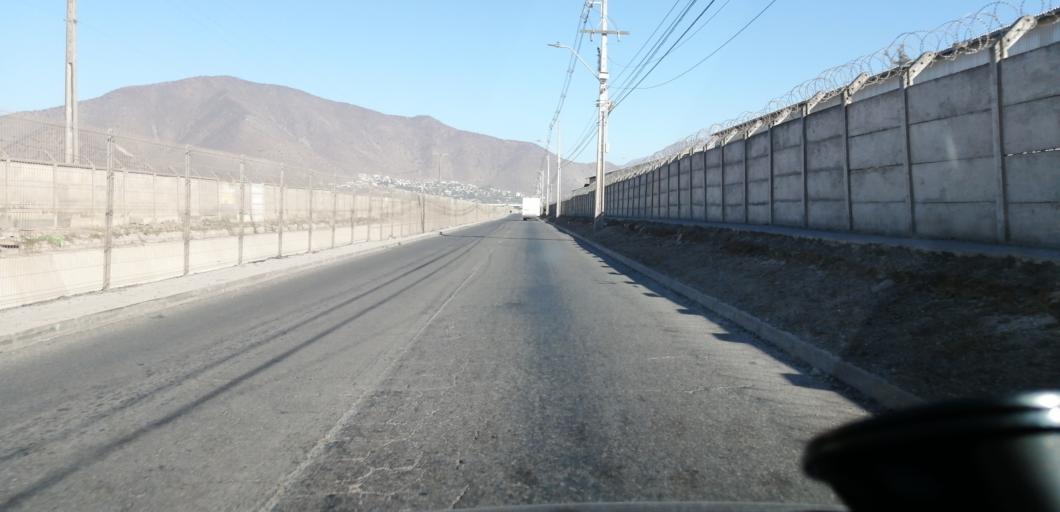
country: CL
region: Santiago Metropolitan
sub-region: Provincia de Santiago
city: Lo Prado
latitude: -33.4570
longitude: -70.7898
